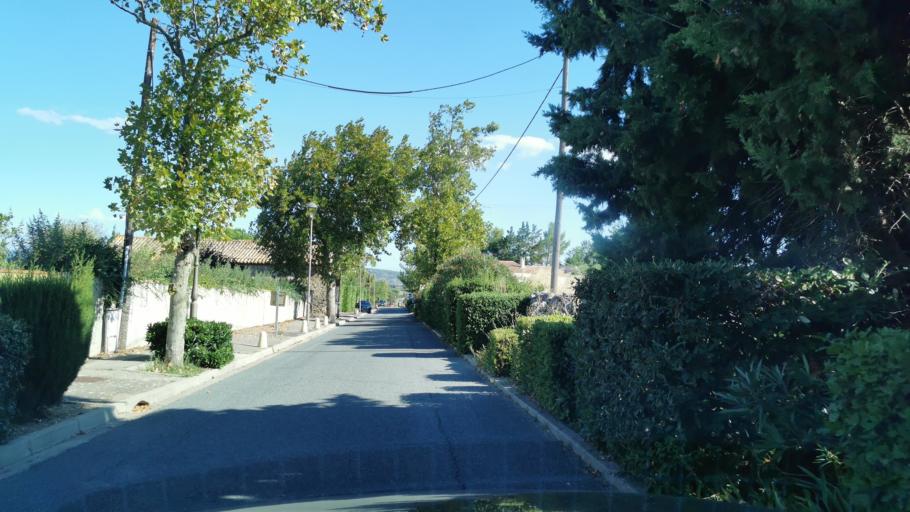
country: FR
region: Languedoc-Roussillon
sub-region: Departement de l'Aude
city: Ginestas
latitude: 43.2752
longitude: 2.8428
